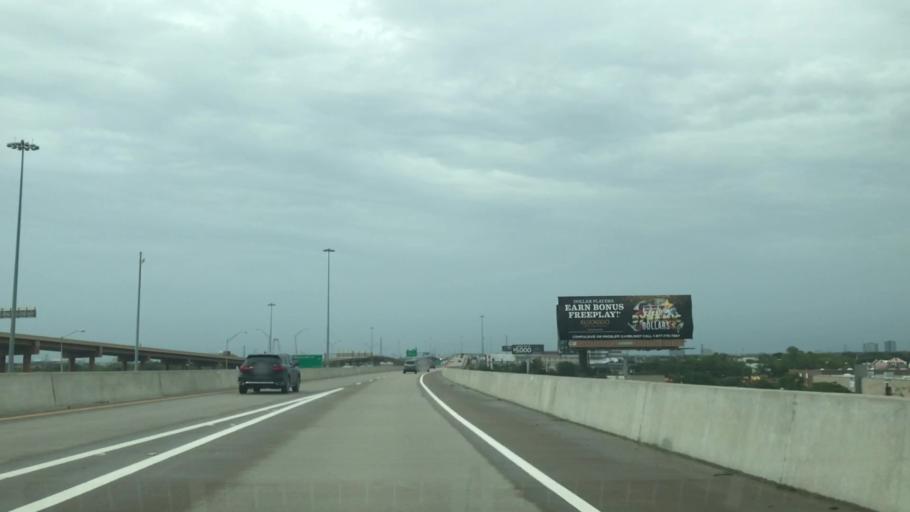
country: US
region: Texas
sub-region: Dallas County
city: Farmers Branch
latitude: 32.8717
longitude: -96.8975
